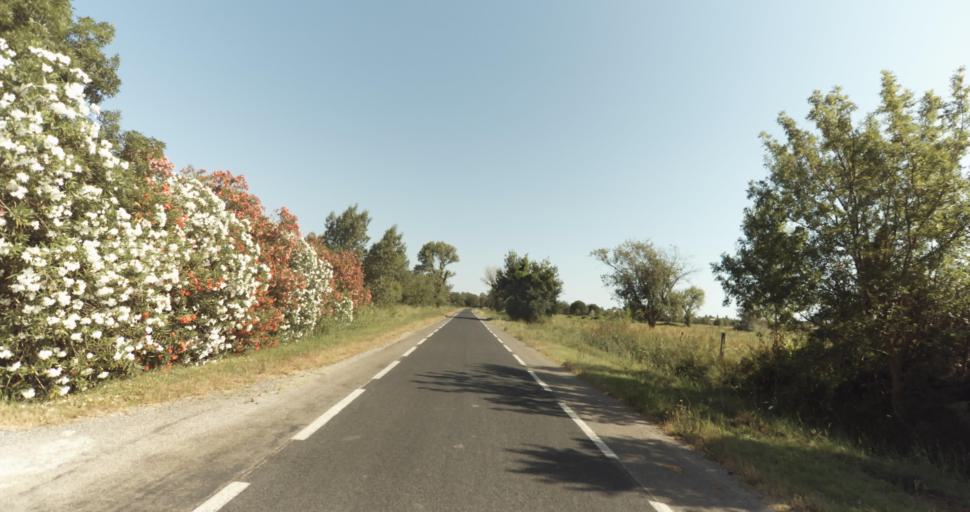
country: FR
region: Languedoc-Roussillon
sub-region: Departement des Pyrenees-Orientales
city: Saint-Cyprien-Plage
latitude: 42.6278
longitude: 3.0192
